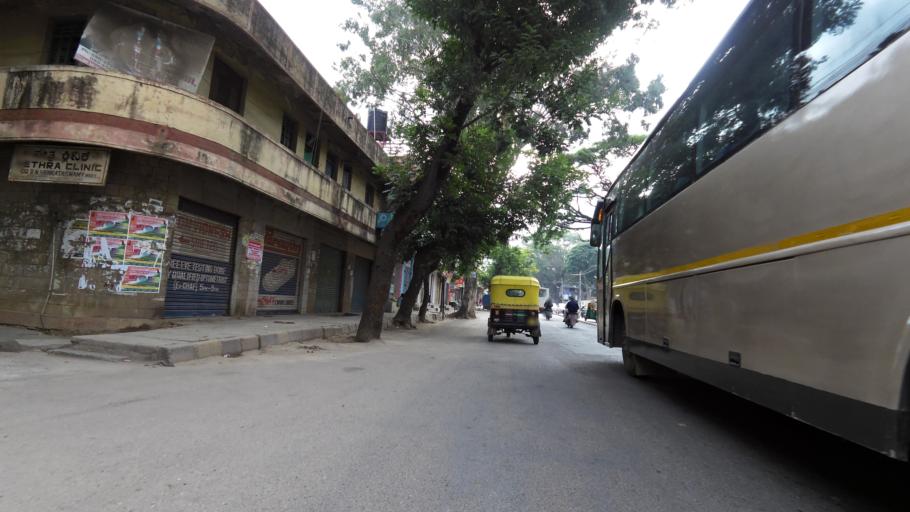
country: IN
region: Karnataka
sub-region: Bangalore Urban
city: Bangalore
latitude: 13.0019
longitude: 77.6322
